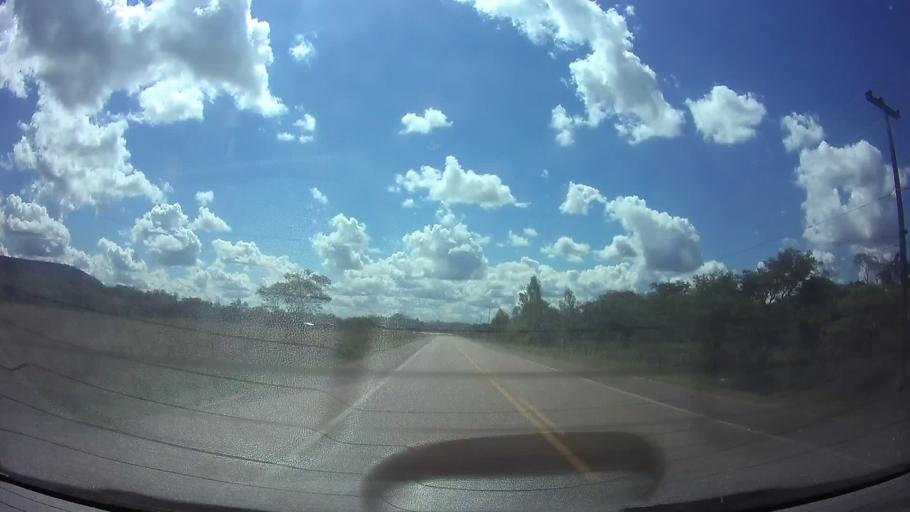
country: PY
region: Guaira
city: Itape
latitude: -25.9165
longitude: -56.7067
